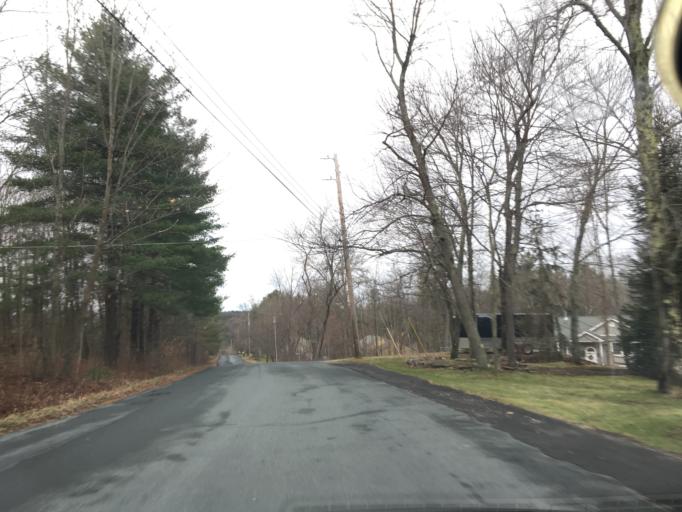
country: US
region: New York
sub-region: Rensselaer County
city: Averill Park
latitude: 42.6138
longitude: -73.5602
